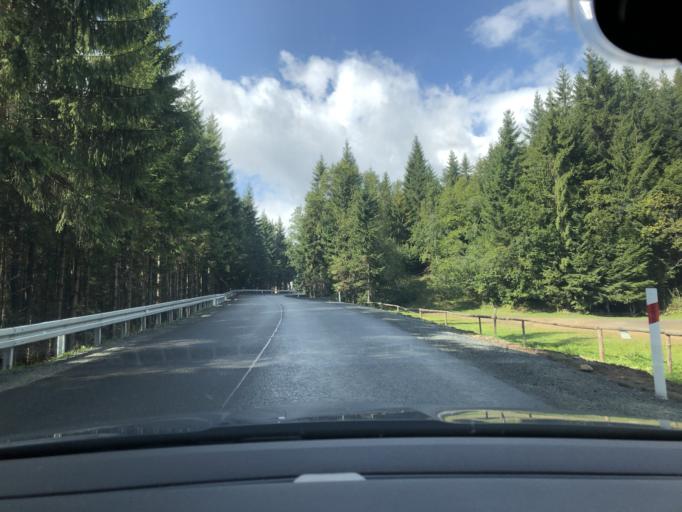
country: PL
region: Lesser Poland Voivodeship
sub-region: Powiat nowotarski
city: Zubrzyca Gorna
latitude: 49.5875
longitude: 19.5851
